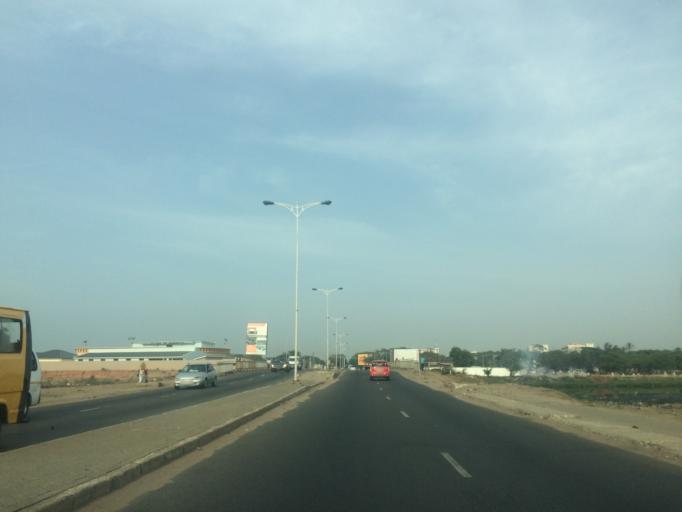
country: GH
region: Greater Accra
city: Accra
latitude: 5.5378
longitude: -0.2188
